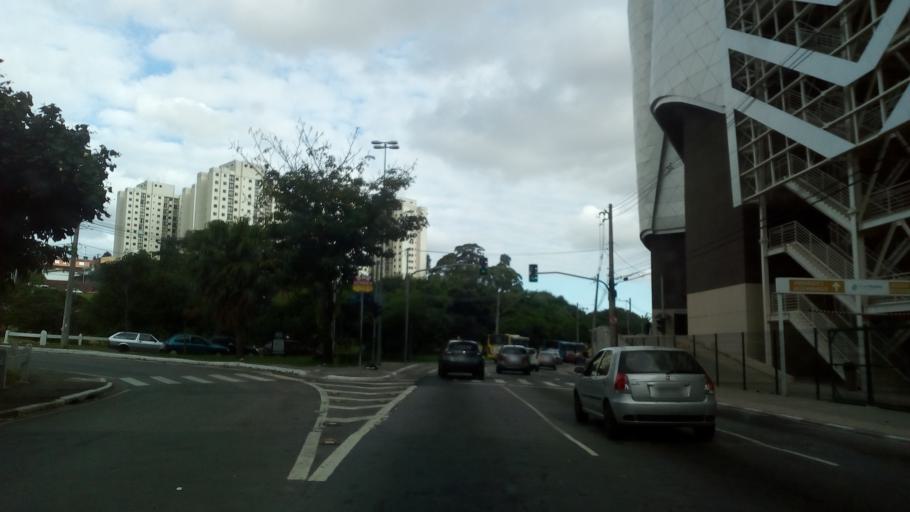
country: BR
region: Sao Paulo
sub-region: Guarulhos
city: Guarulhos
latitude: -23.4426
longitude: -46.5404
